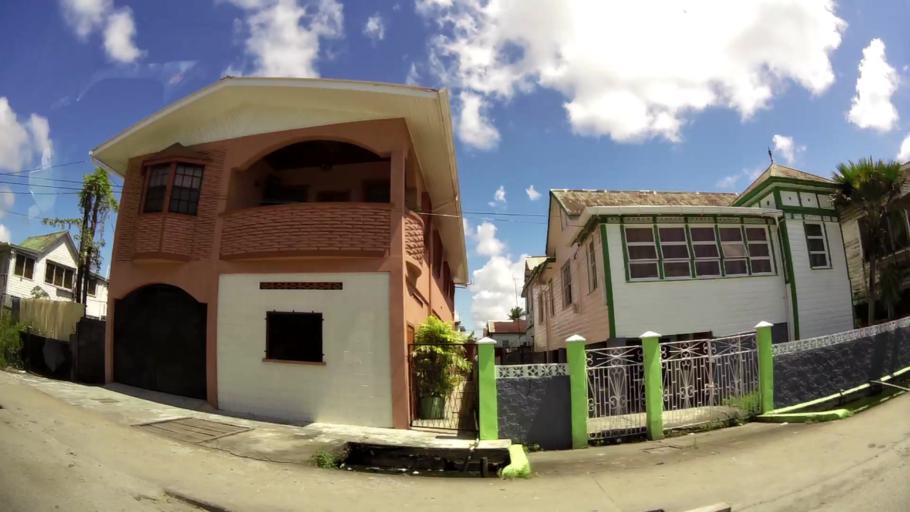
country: GY
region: Demerara-Mahaica
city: Georgetown
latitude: 6.8030
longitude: -58.1531
